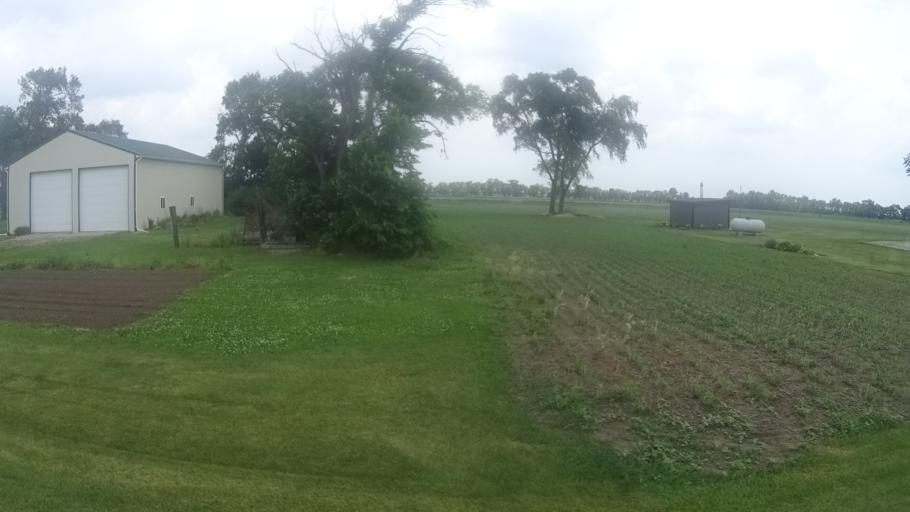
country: US
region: Ohio
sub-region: Huron County
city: Monroeville
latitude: 41.3074
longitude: -82.7102
